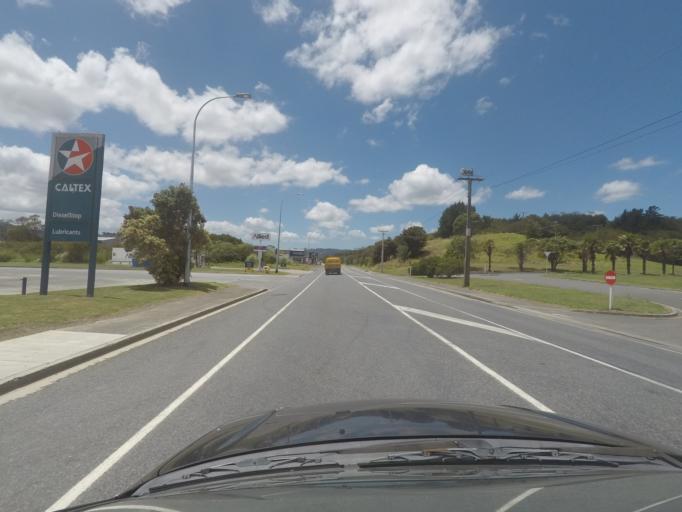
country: NZ
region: Northland
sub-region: Whangarei
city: Whangarei
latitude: -35.7439
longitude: 174.3282
